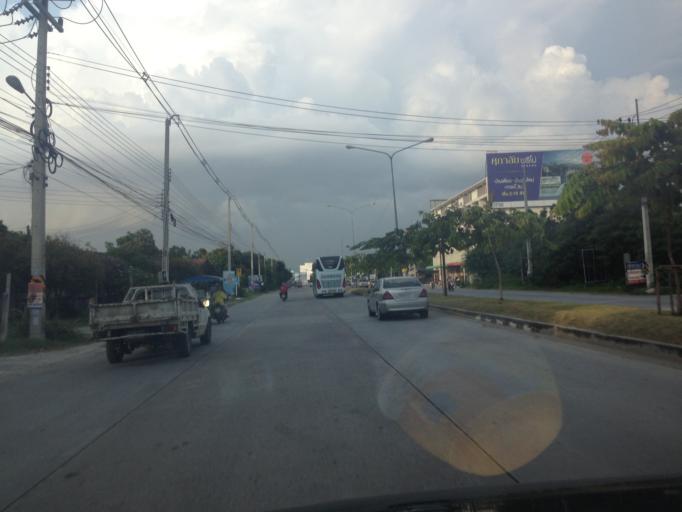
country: TH
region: Chon Buri
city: Chon Buri
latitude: 13.2946
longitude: 100.9176
